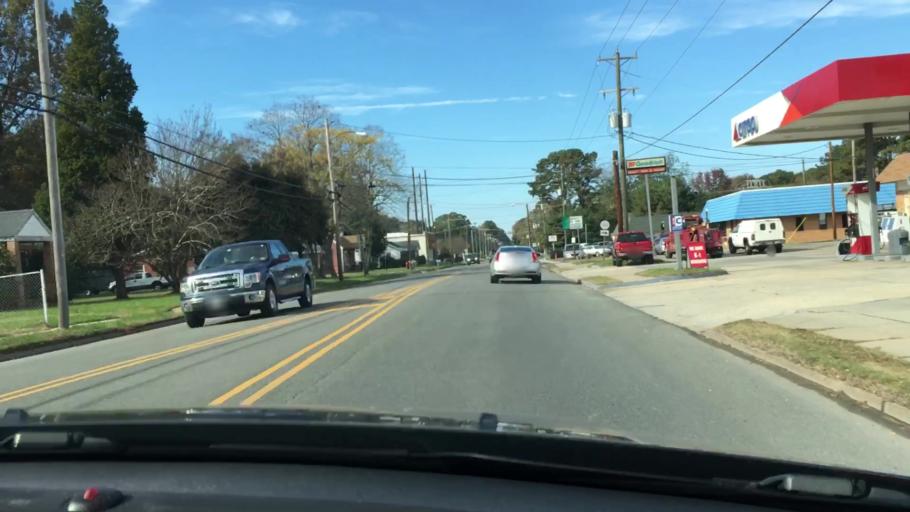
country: US
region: Virginia
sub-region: King William County
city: West Point
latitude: 37.5516
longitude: -76.8106
